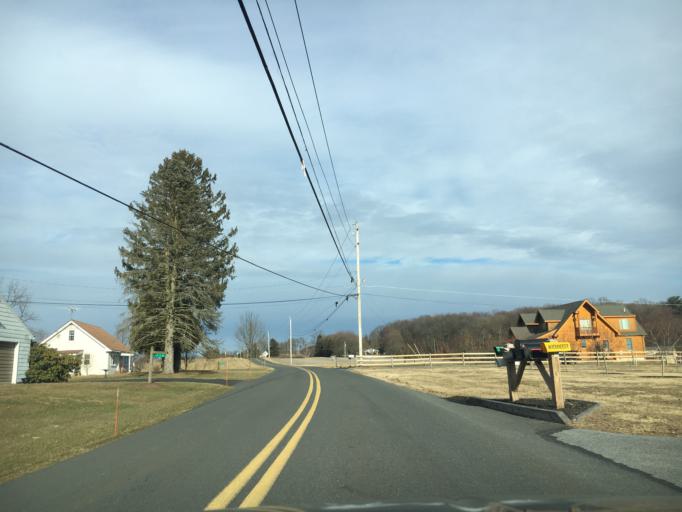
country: US
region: Pennsylvania
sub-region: Berks County
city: Stony Creek Mills
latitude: 40.3791
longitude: -75.8430
